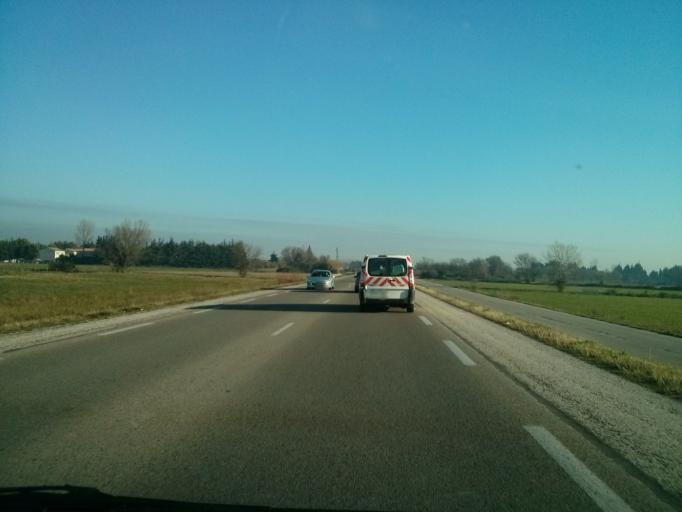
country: FR
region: Languedoc-Roussillon
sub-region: Departement du Gard
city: Uchaud
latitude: 43.7548
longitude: 4.2756
